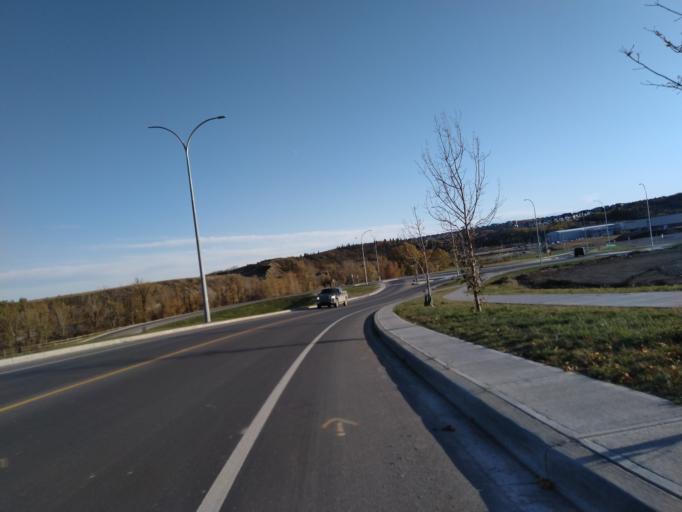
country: CA
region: Alberta
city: Cochrane
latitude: 51.1820
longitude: -114.4509
